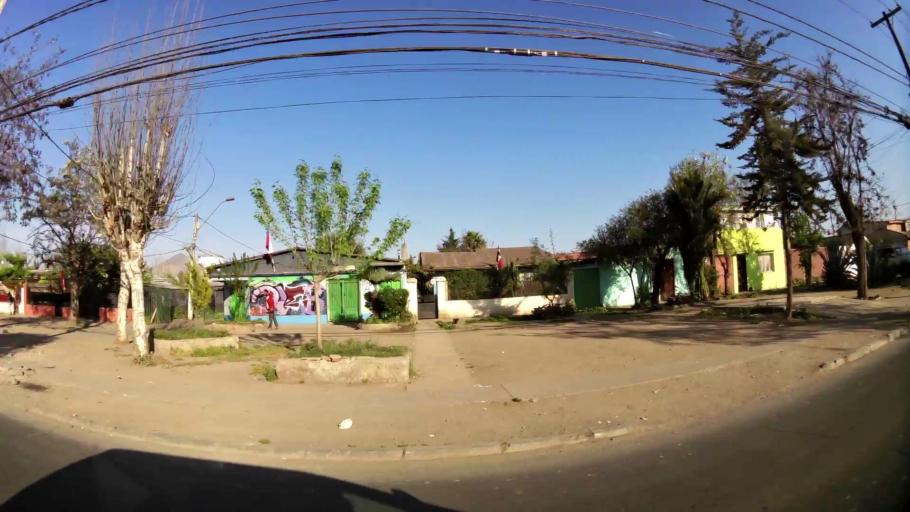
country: CL
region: Santiago Metropolitan
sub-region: Provincia de Santiago
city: Santiago
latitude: -33.3774
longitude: -70.6719
